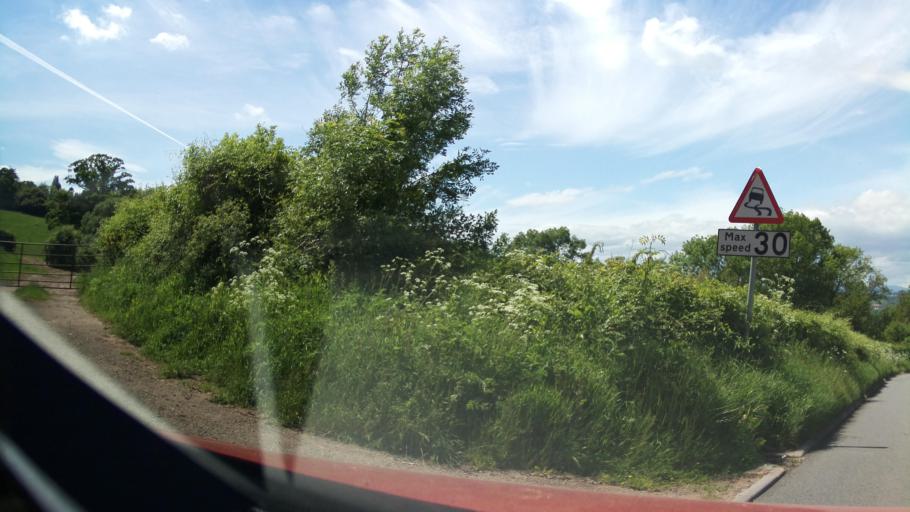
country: GB
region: Wales
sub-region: Monmouthshire
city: Mitchel Troy
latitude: 51.7875
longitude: -2.7178
